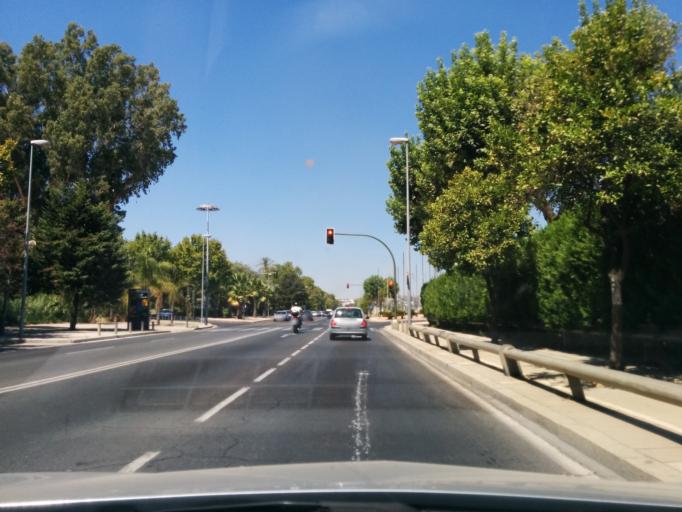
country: ES
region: Andalusia
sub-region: Provincia de Sevilla
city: Sevilla
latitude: 37.3687
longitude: -6.0031
